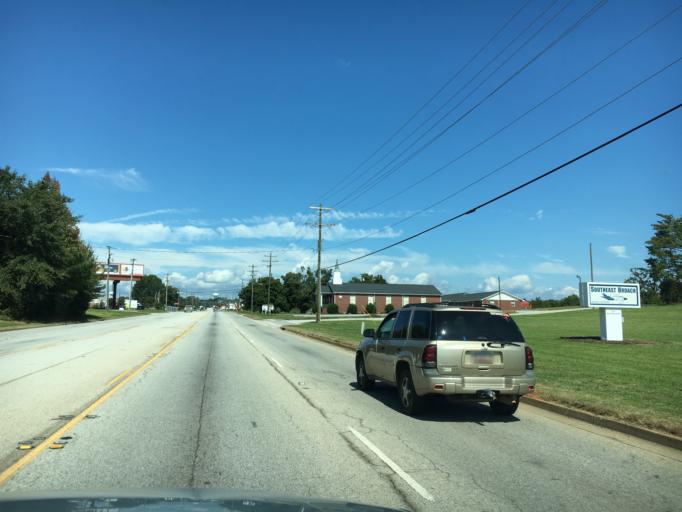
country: US
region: South Carolina
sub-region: Greenville County
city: Greer
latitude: 34.9322
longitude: -82.2508
